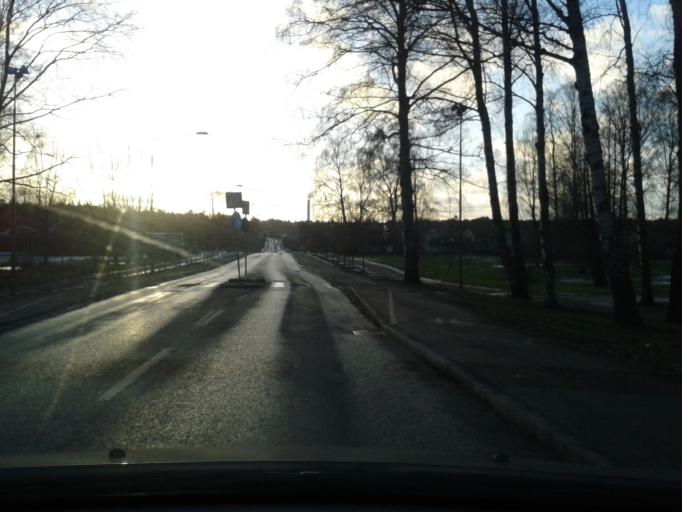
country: SE
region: Stockholm
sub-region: Stockholms Kommun
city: Arsta
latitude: 59.2708
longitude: 18.0919
